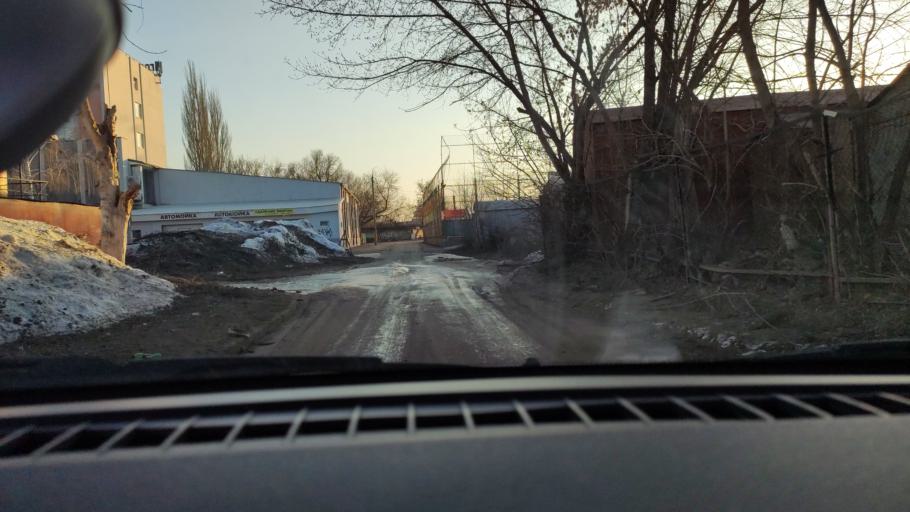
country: RU
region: Samara
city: Smyshlyayevka
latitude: 53.2161
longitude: 50.2748
